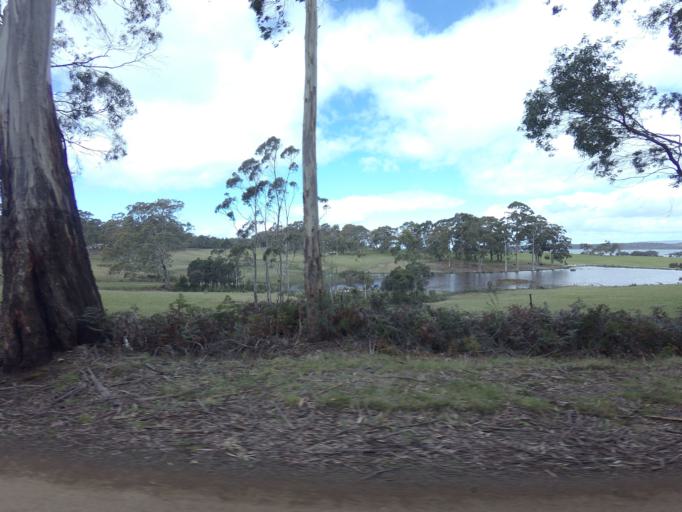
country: AU
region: Tasmania
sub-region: Huon Valley
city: Geeveston
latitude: -43.4259
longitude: 146.9980
